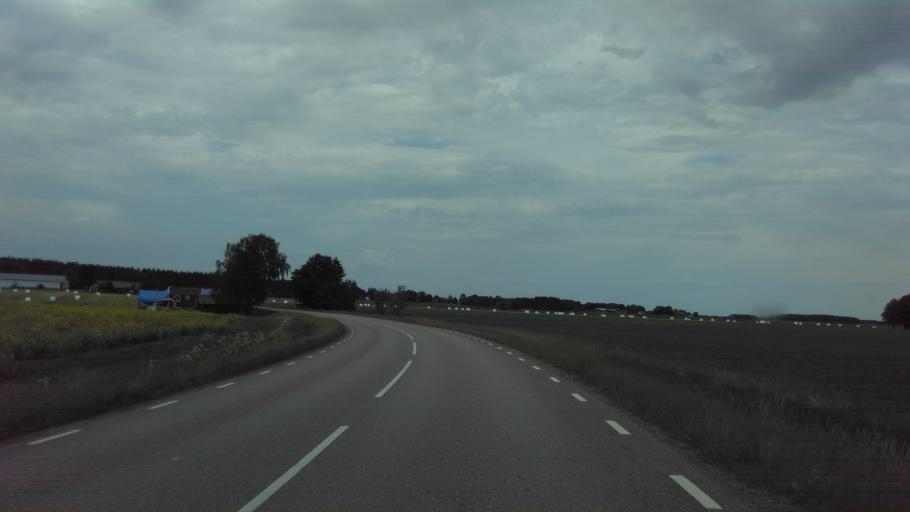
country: SE
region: Vaestra Goetaland
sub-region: Lidkopings Kommun
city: Lidkoping
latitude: 58.4257
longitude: 13.1611
